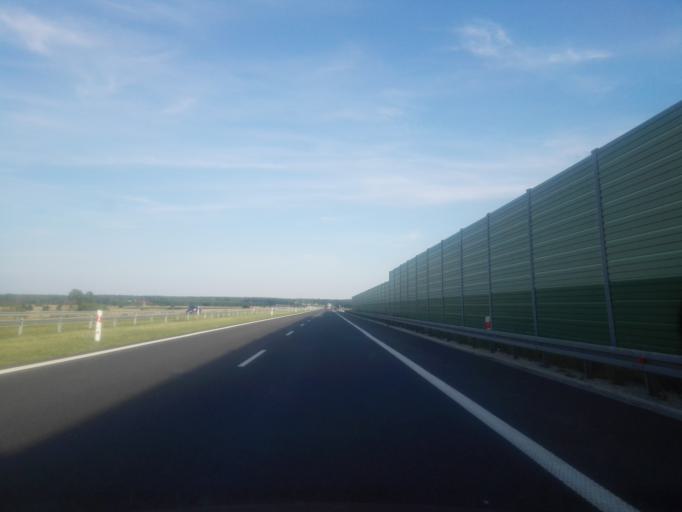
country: PL
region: Lodz Voivodeship
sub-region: Powiat wieruszowski
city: Wieruszow
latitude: 51.3244
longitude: 18.1556
